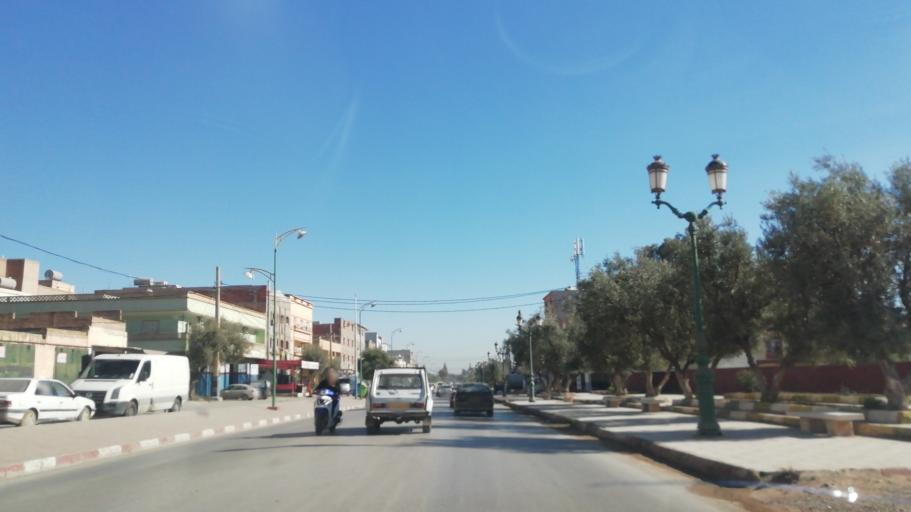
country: DZ
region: Tlemcen
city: Nedroma
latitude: 34.8450
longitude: -1.7485
